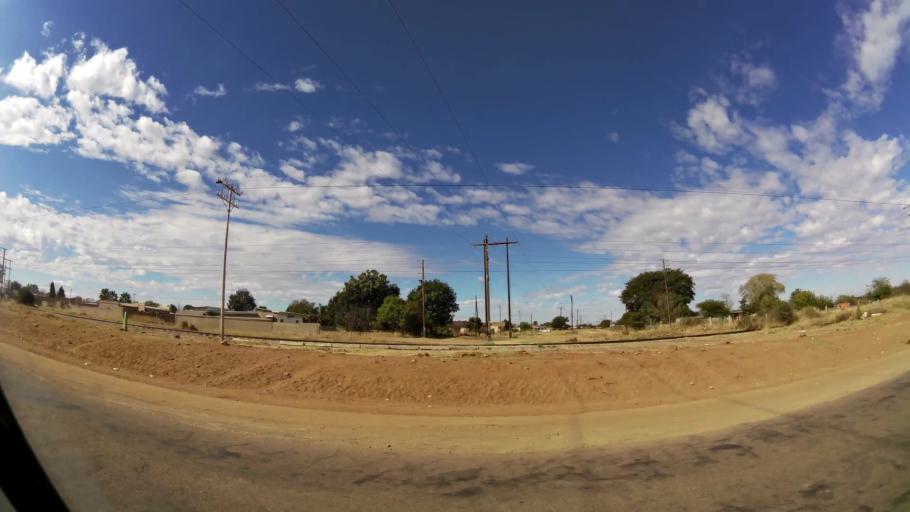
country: ZA
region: Limpopo
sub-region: Waterberg District Municipality
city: Bela-Bela
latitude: -24.8737
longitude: 28.3173
